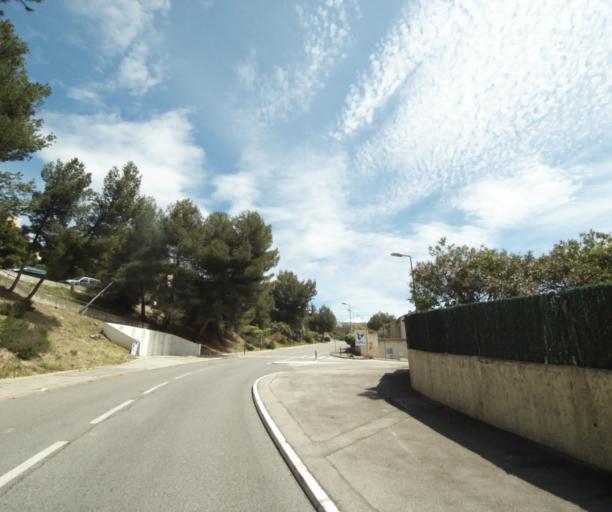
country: FR
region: Provence-Alpes-Cote d'Azur
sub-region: Departement des Bouches-du-Rhone
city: Rognac
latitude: 43.4949
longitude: 5.2324
